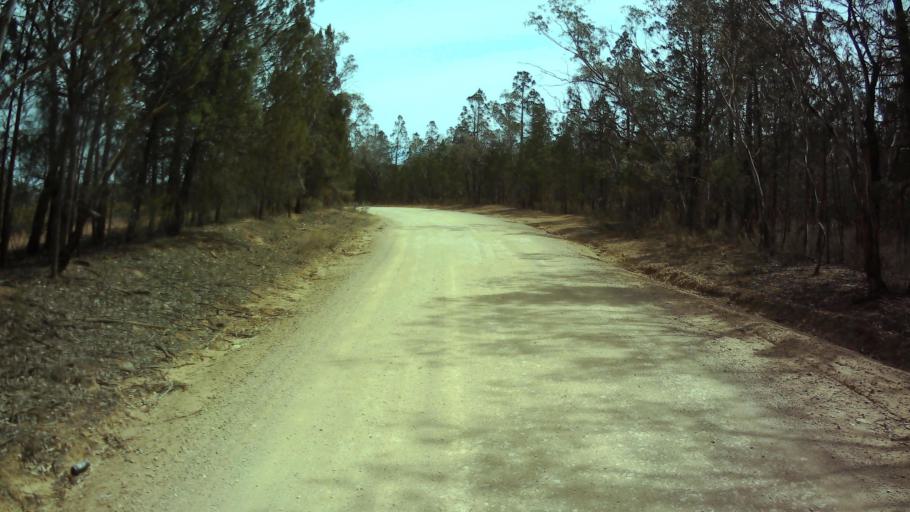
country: AU
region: New South Wales
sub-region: Weddin
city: Grenfell
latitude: -33.9118
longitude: 148.4126
